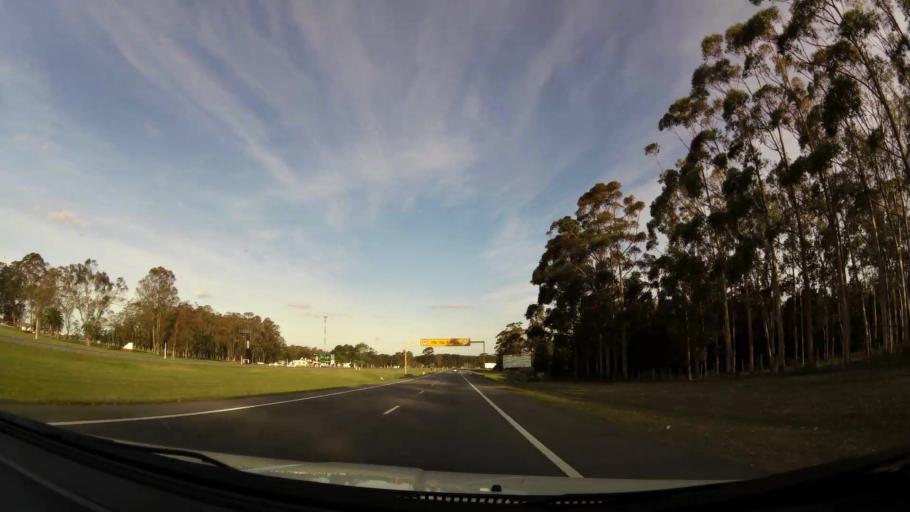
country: UY
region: Maldonado
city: Maldonado
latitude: -34.8670
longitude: -55.0866
